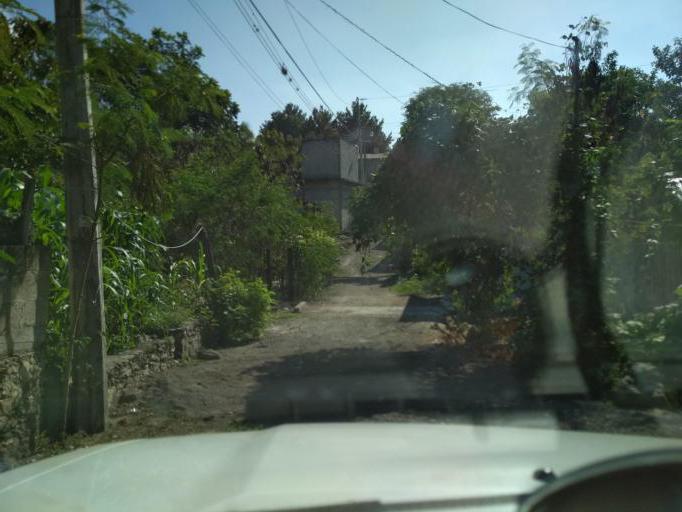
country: MX
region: Veracruz
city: Rinconada
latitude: 19.3563
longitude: -96.5611
